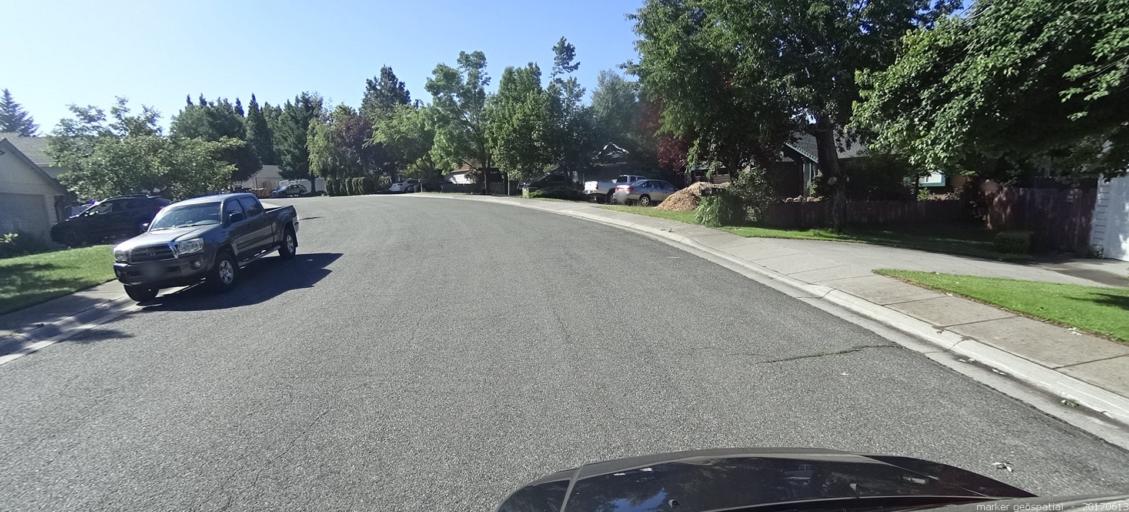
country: US
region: California
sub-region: Siskiyou County
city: Mount Shasta
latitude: 41.3024
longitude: -122.3054
